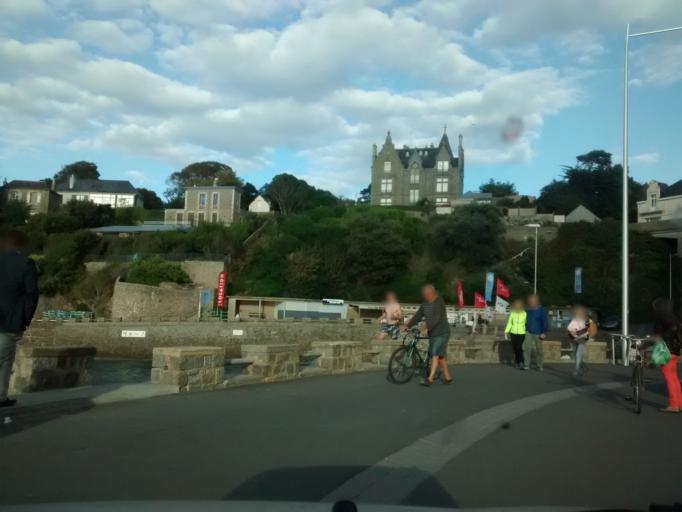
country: FR
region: Brittany
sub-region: Departement d'Ille-et-Vilaine
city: Dinard
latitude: 48.6369
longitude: -2.0504
